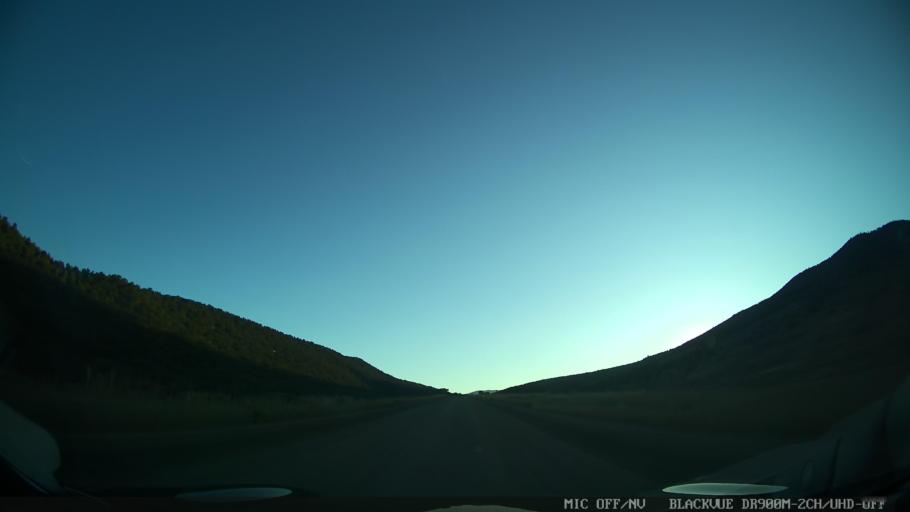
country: US
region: Colorado
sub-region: Grand County
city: Kremmling
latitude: 39.9100
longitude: -106.5726
